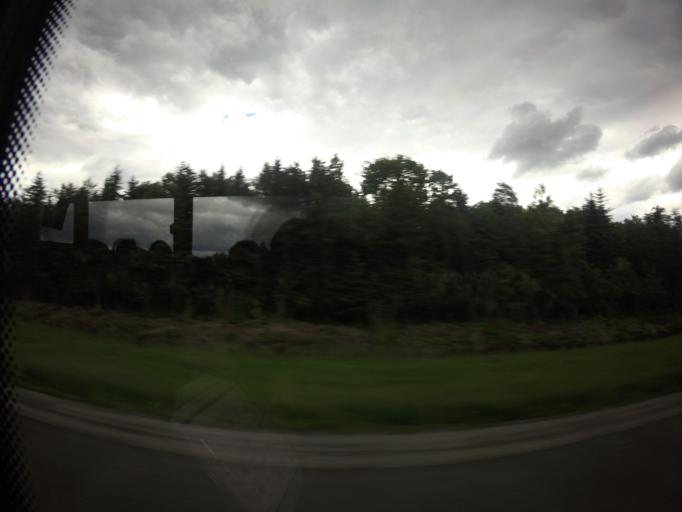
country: CA
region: Quebec
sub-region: Chaudiere-Appalaches
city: Saint-Antoine-de-Tilly
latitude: 46.5090
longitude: -71.6642
